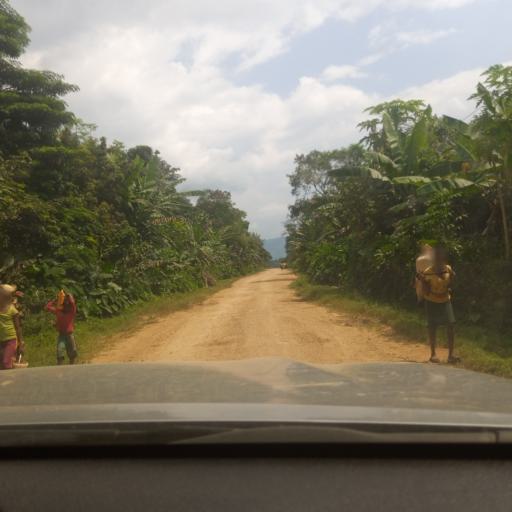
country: ET
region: Southern Nations, Nationalities, and People's Region
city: Tippi
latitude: 7.1347
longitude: 35.4245
